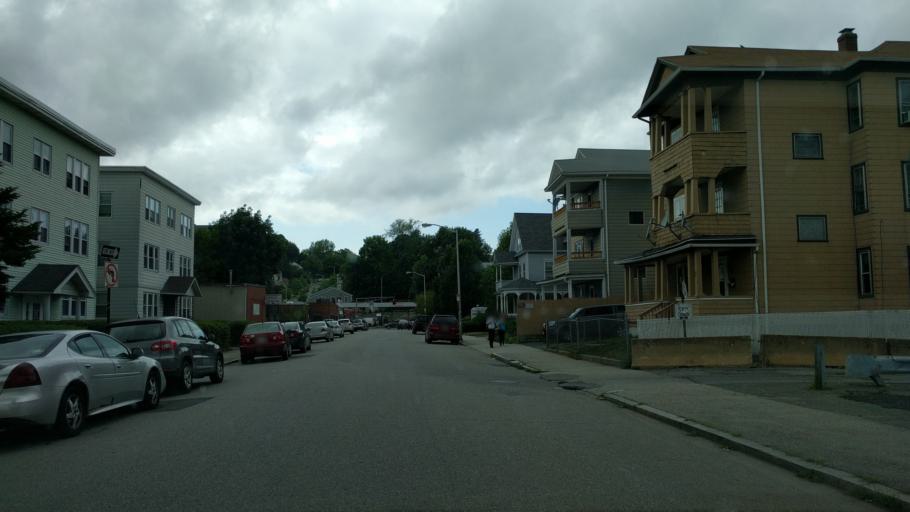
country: US
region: Massachusetts
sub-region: Worcester County
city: Worcester
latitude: 42.2905
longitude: -71.8045
